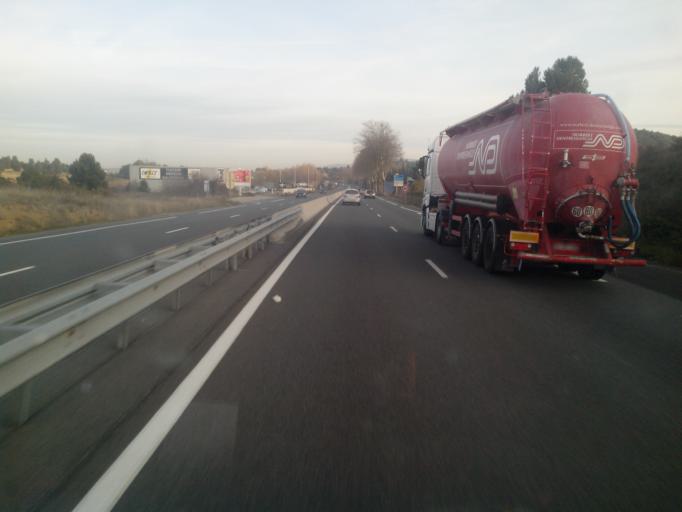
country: FR
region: Languedoc-Roussillon
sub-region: Departement de l'Aude
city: Palaja
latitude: 43.2061
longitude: 2.3925
